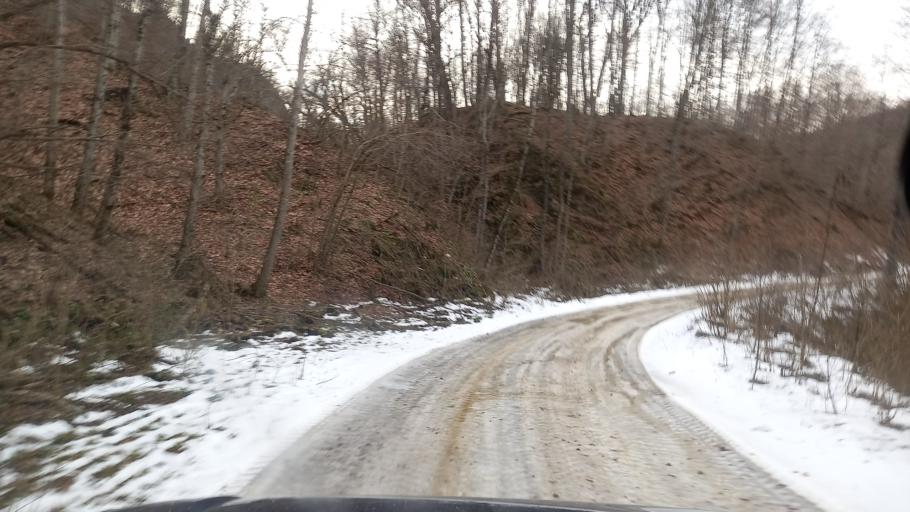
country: RU
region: Adygeya
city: Kamennomostskiy
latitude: 44.1532
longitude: 40.3013
